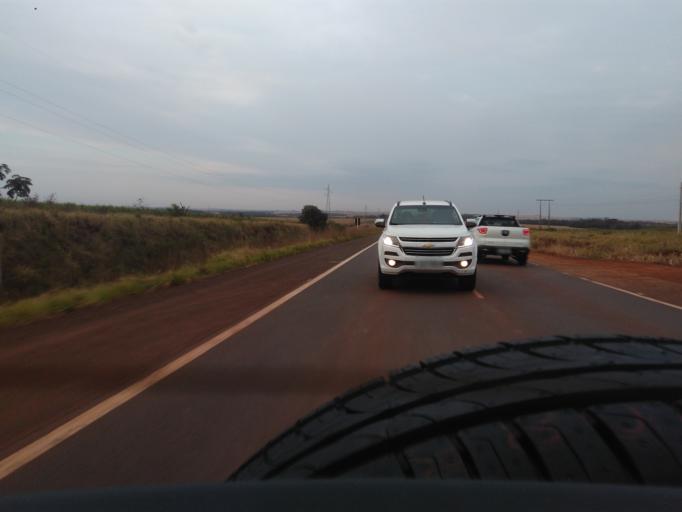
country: BR
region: Mato Grosso do Sul
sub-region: Dourados
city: Dourados
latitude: -22.2989
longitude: -55.0869
